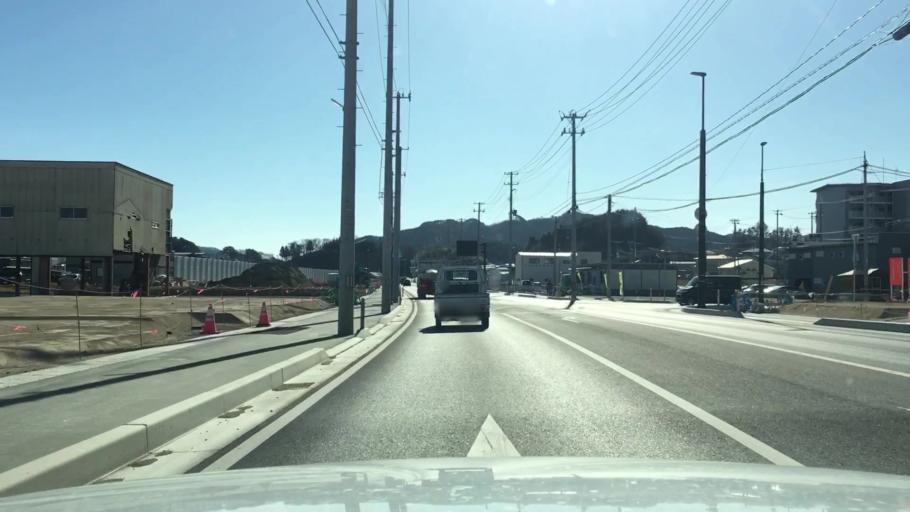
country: JP
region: Iwate
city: Yamada
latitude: 39.4650
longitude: 141.9528
